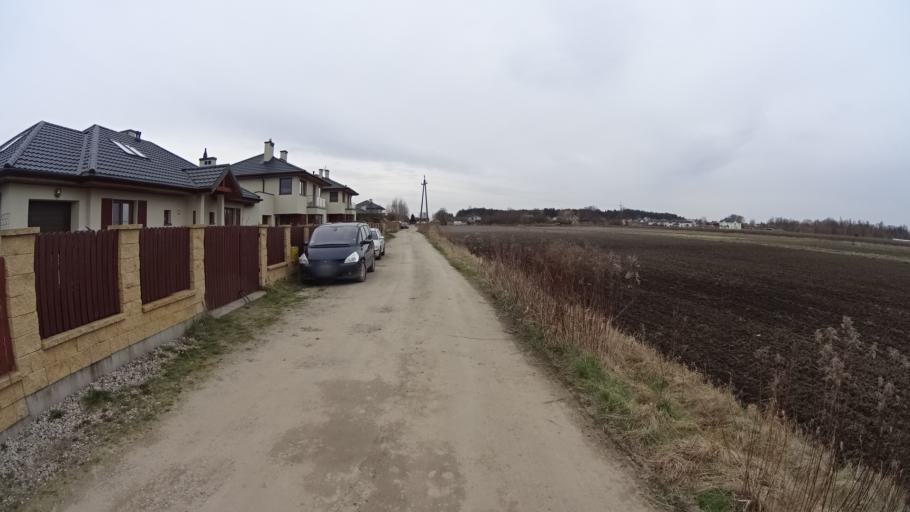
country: PL
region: Masovian Voivodeship
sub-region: Powiat warszawski zachodni
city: Hornowek
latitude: 52.2683
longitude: 20.7895
